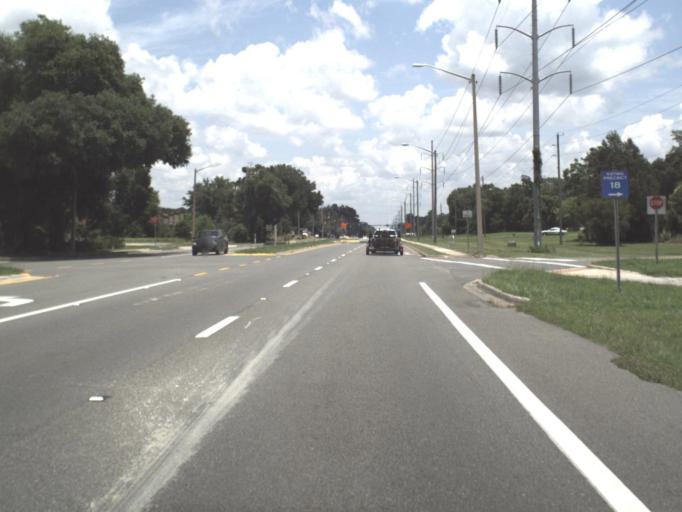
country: US
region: Florida
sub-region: Alachua County
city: Gainesville
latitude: 29.5973
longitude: -82.4241
